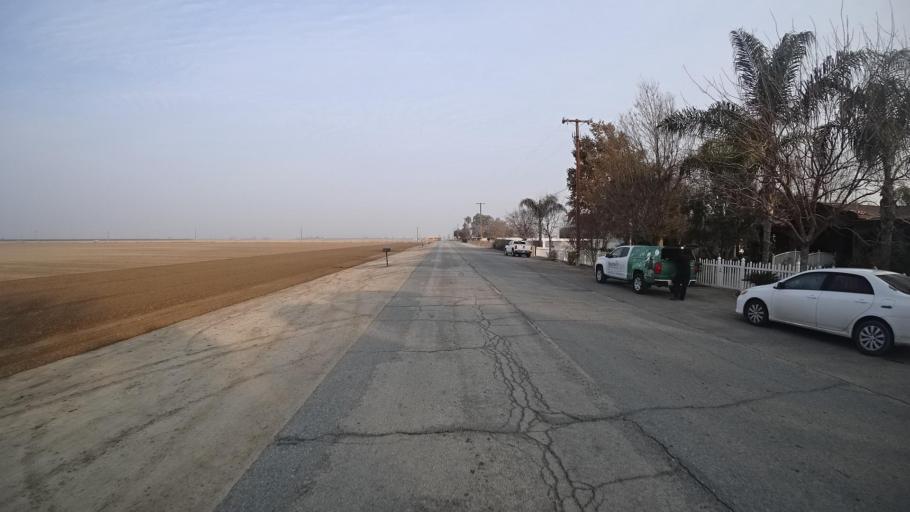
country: US
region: California
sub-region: Kern County
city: Greenfield
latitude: 35.2352
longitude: -119.0211
